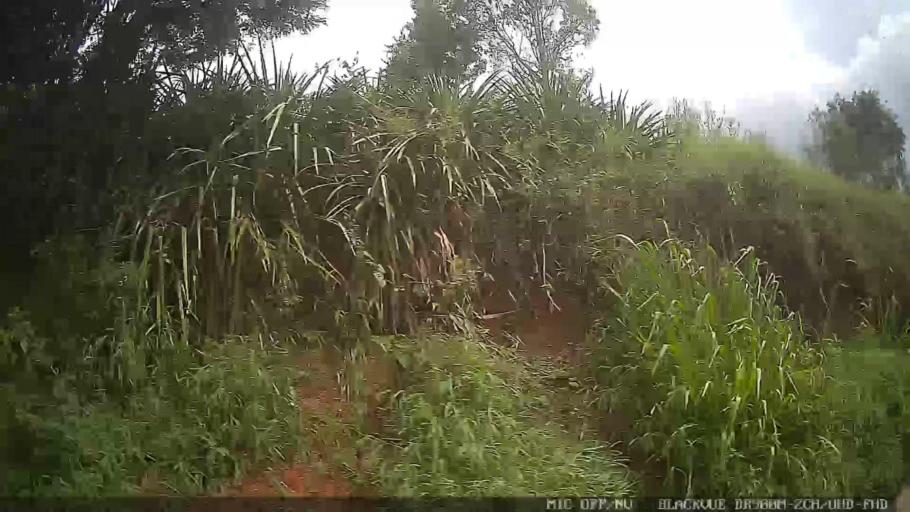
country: BR
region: Minas Gerais
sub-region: Extrema
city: Extrema
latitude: -22.7601
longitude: -46.3300
